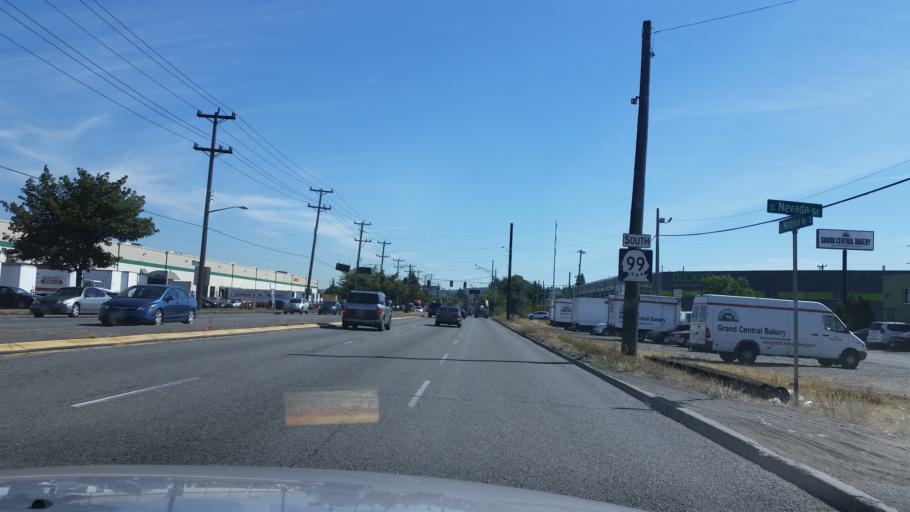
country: US
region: Washington
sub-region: King County
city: Seattle
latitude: 47.5658
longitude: -122.3395
